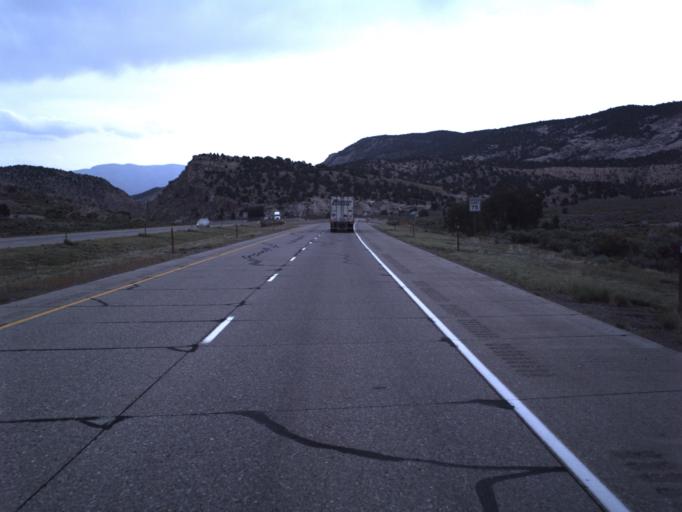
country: US
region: Utah
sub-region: Sevier County
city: Monroe
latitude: 38.5761
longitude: -112.3397
